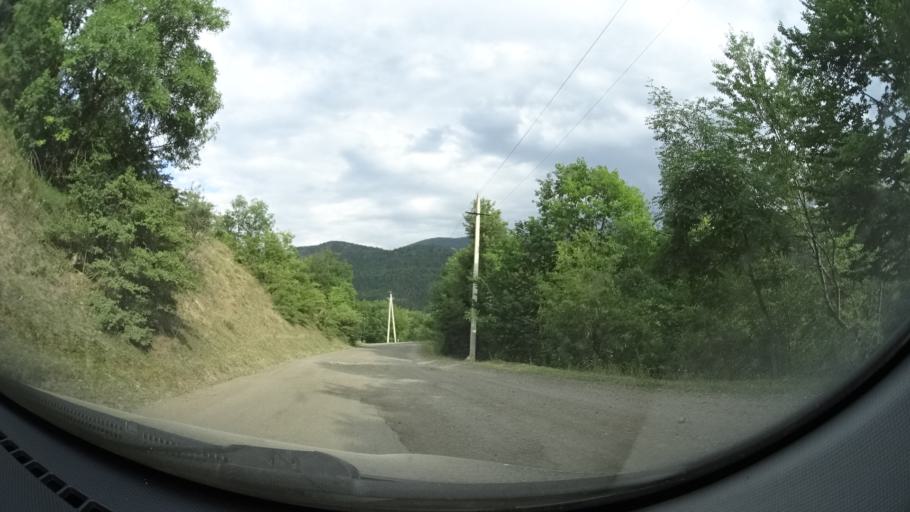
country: GE
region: Samtskhe-Javakheti
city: Adigeni
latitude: 41.6672
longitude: 42.6235
